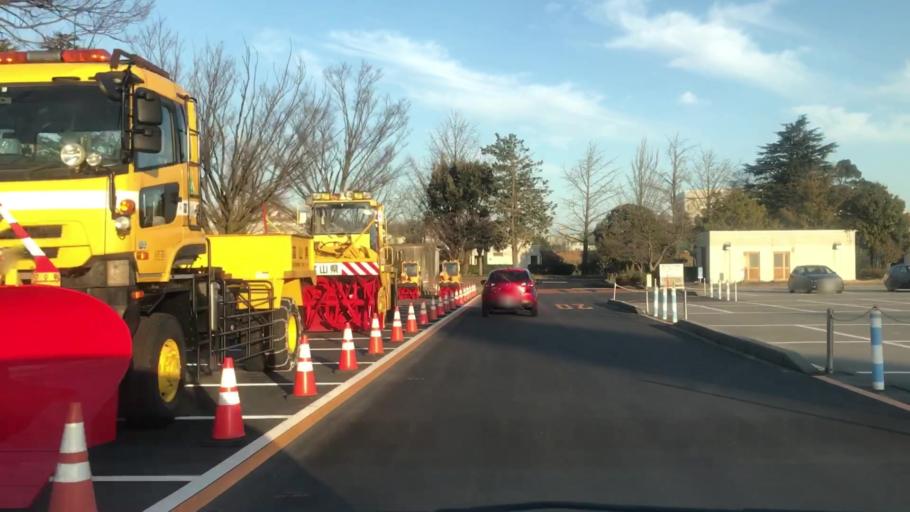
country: JP
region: Toyama
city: Toyama-shi
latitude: 36.6956
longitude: 137.1899
